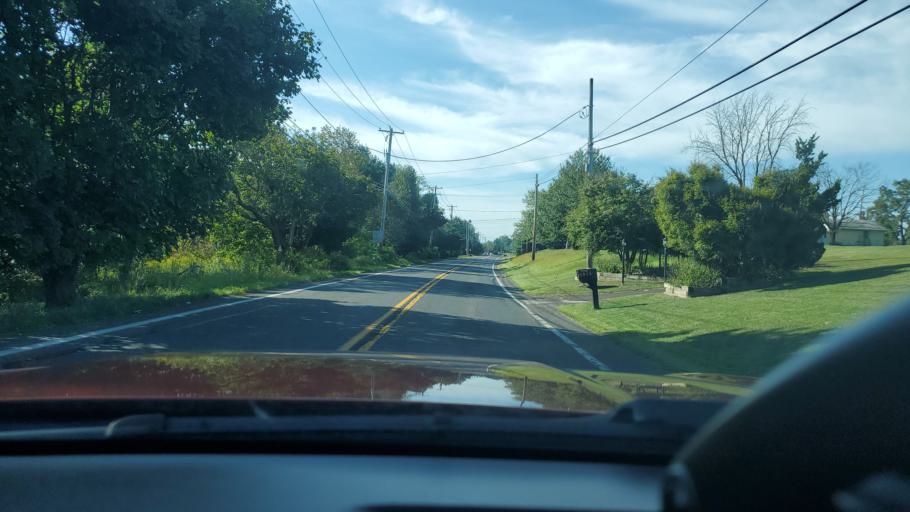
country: US
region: Pennsylvania
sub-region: Montgomery County
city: Limerick
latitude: 40.2995
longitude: -75.5248
